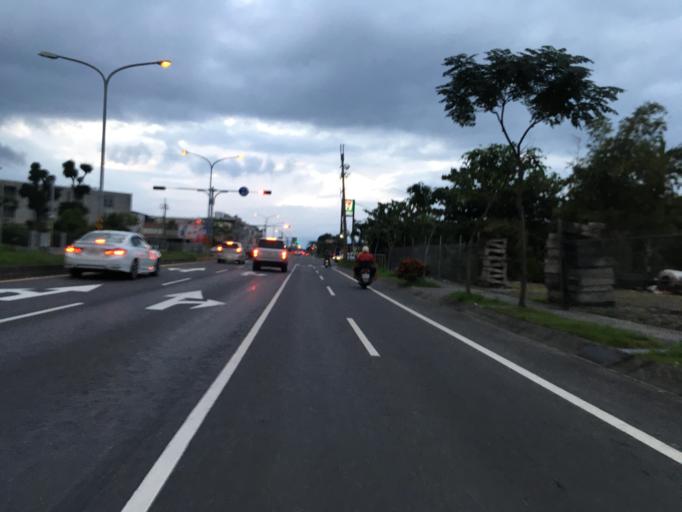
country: TW
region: Taiwan
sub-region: Yilan
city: Yilan
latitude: 24.6231
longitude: 121.8386
